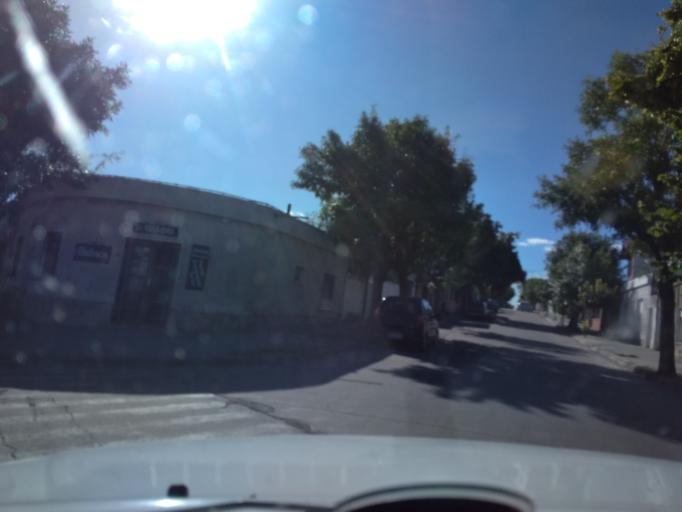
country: UY
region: Florida
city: Florida
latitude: -34.0997
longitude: -56.2188
